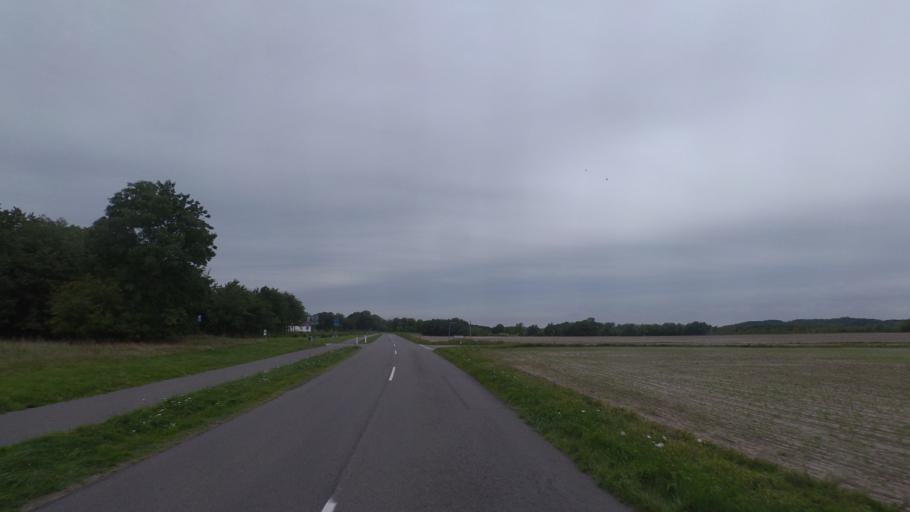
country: DK
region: Capital Region
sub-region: Bornholm Kommune
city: Nexo
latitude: 55.0036
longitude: 15.0388
